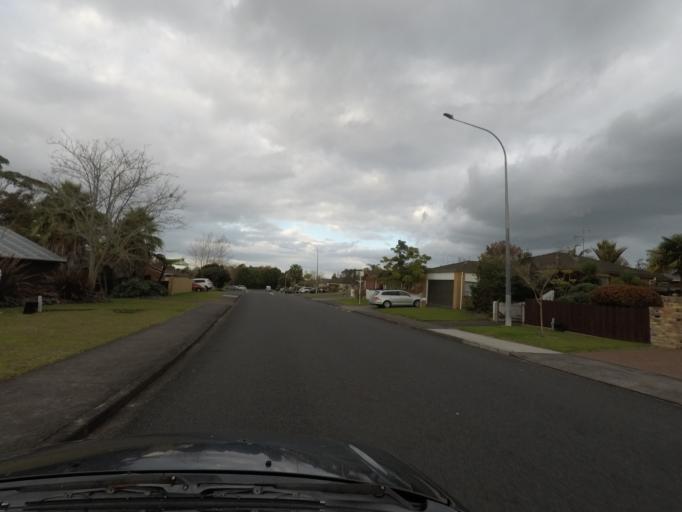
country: NZ
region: Auckland
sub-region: Auckland
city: Rosebank
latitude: -36.8289
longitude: 174.6269
